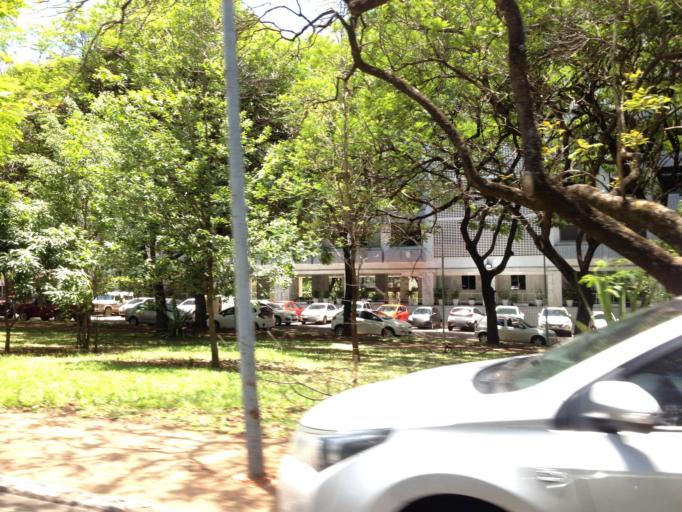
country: BR
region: Federal District
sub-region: Brasilia
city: Brasilia
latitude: -15.8177
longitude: -47.9073
